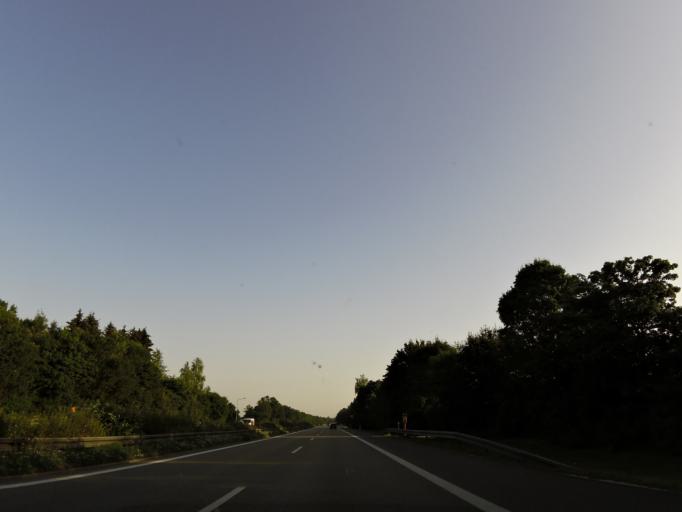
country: DE
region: Bavaria
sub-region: Swabia
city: Illertissen
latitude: 48.2400
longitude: 10.1204
